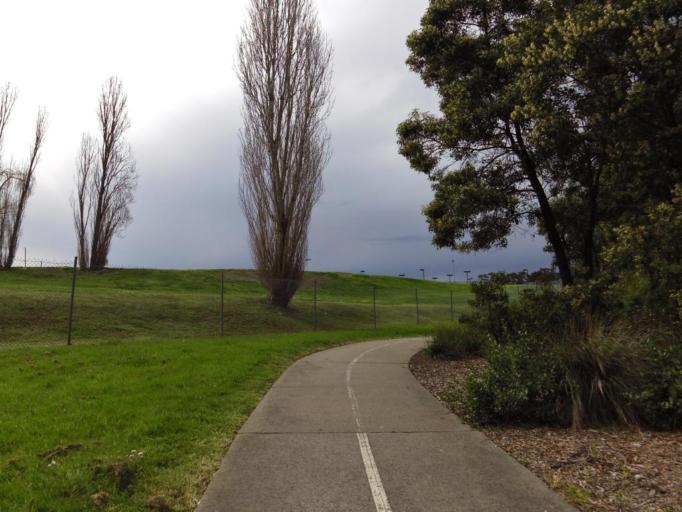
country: AU
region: Victoria
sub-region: Maroondah
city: Croydon Hills
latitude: -37.7866
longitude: 145.2592
